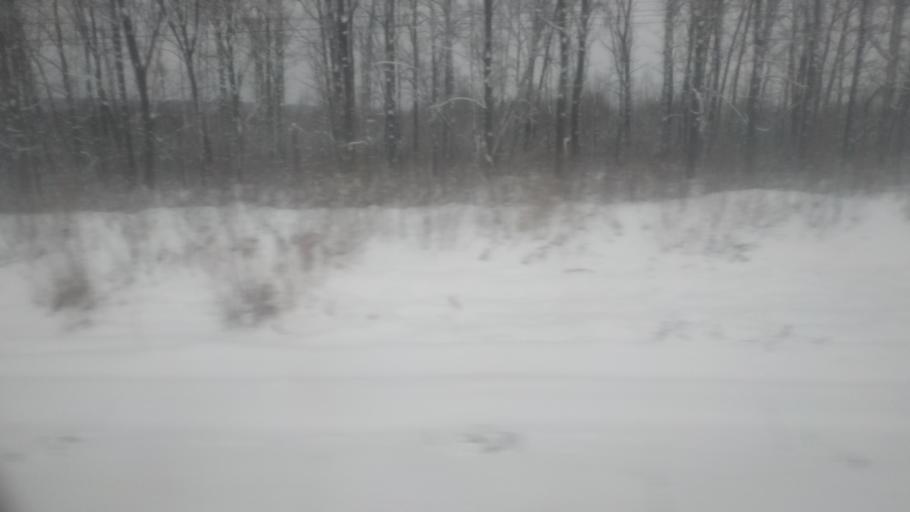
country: RU
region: Bashkortostan
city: Amzya
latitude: 56.2397
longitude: 54.5350
